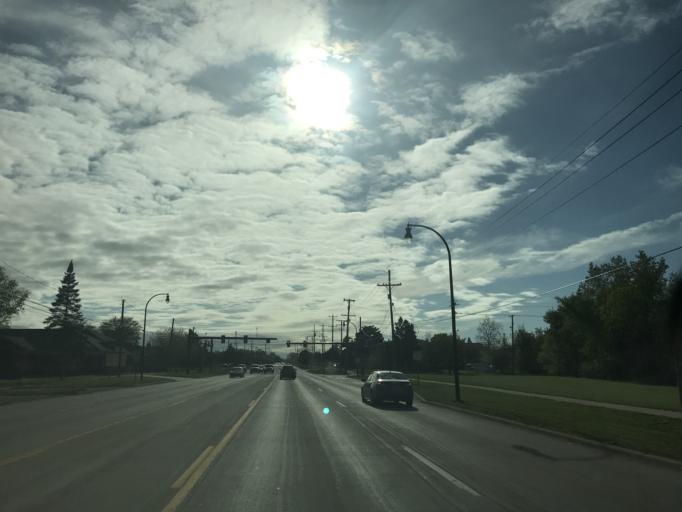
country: US
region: Michigan
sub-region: Wayne County
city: Woodhaven
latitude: 42.1384
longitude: -83.2497
